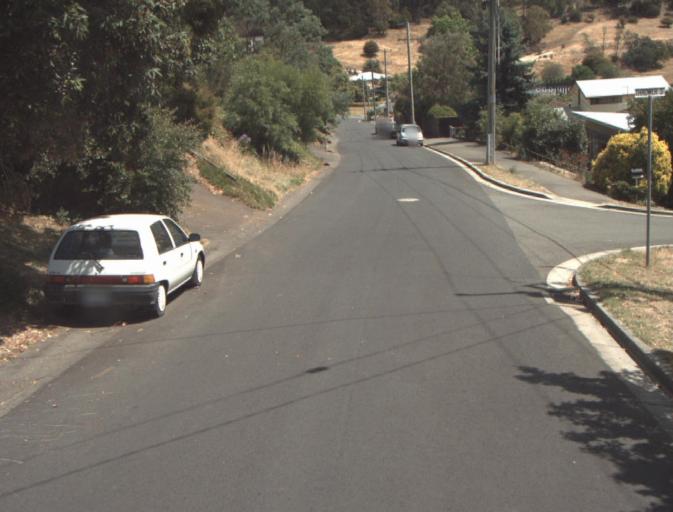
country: AU
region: Tasmania
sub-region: Launceston
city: West Launceston
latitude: -41.4459
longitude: 147.1273
